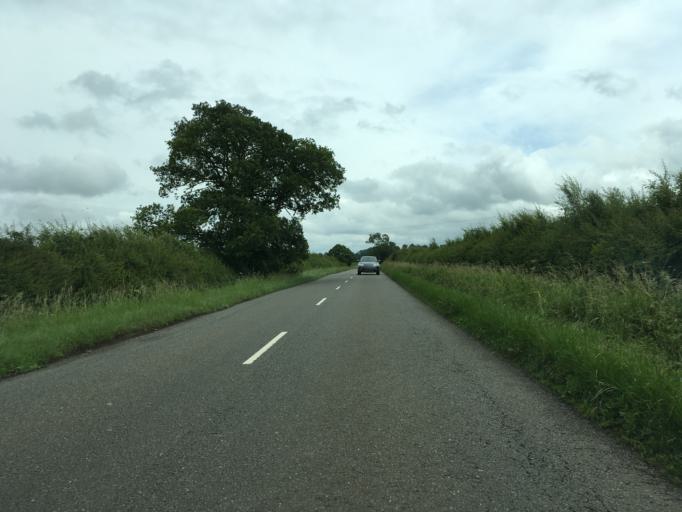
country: GB
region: England
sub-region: Warwickshire
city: Harbury
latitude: 52.2461
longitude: -1.4892
